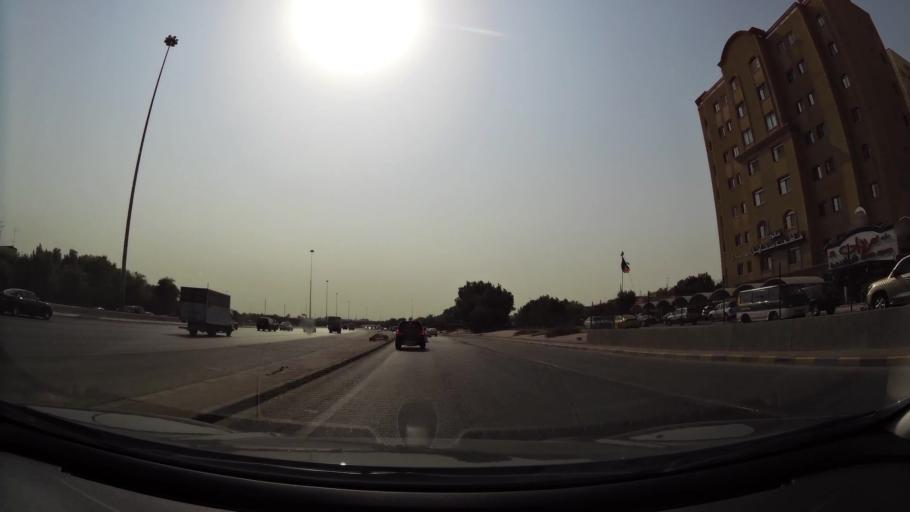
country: KW
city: Bayan
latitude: 29.3183
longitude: 48.0574
